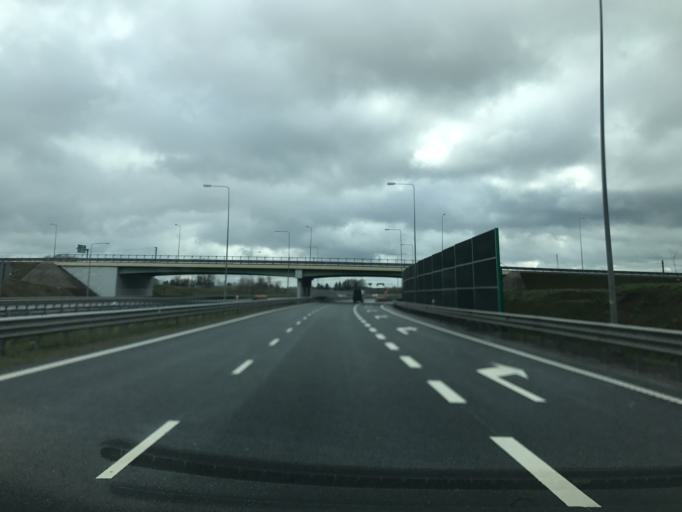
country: PL
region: Warmian-Masurian Voivodeship
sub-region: Powiat olsztynski
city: Olsztynek
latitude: 53.5866
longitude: 20.2553
